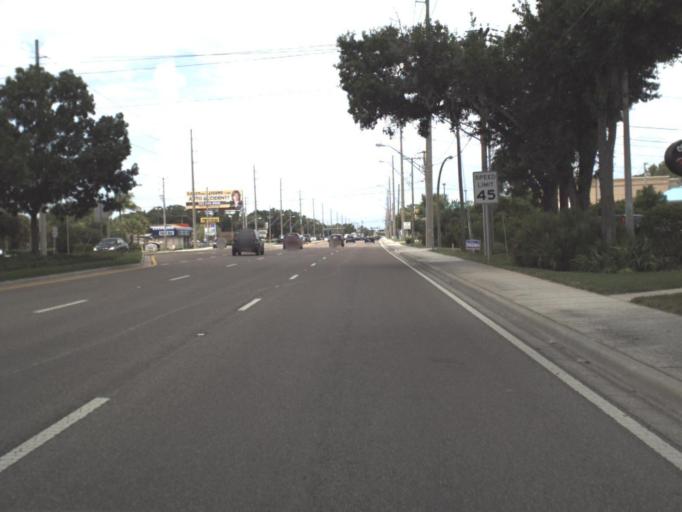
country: US
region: Florida
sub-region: Pinellas County
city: Oldsmar
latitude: 28.0441
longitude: -82.6790
